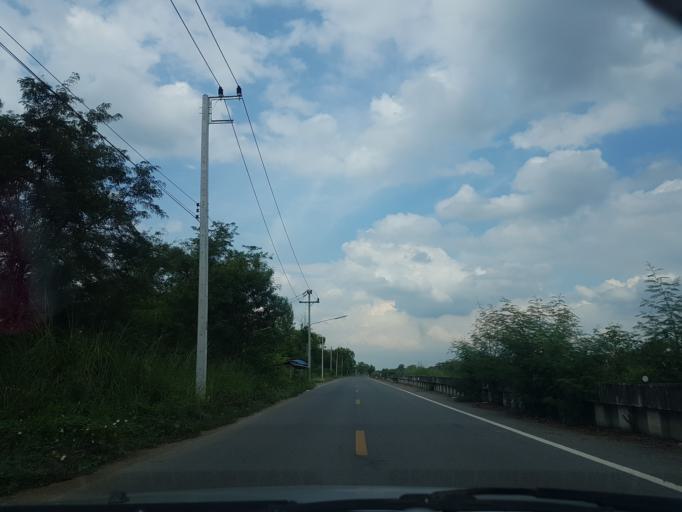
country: TH
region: Pathum Thani
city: Nong Suea
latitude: 14.1866
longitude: 100.8915
